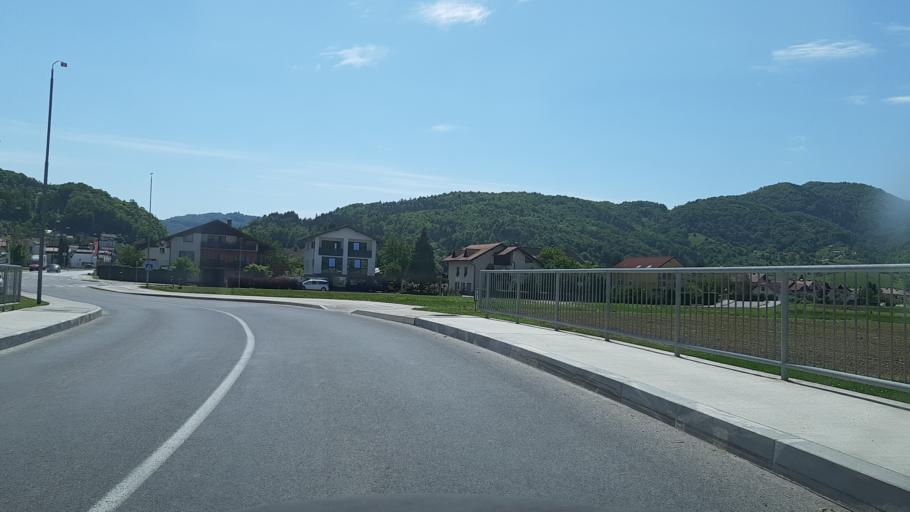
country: SI
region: Sentjur pri Celju
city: Sentjur
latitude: 46.2117
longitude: 15.3927
